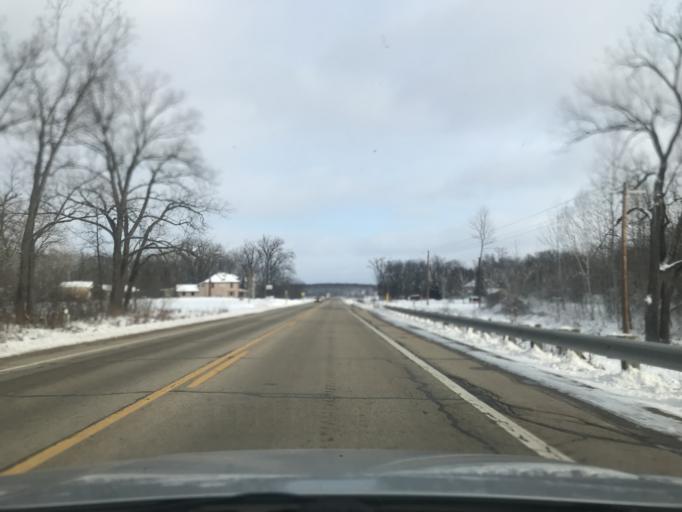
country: US
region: Wisconsin
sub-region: Oconto County
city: Oconto Falls
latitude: 44.8880
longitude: -88.0140
